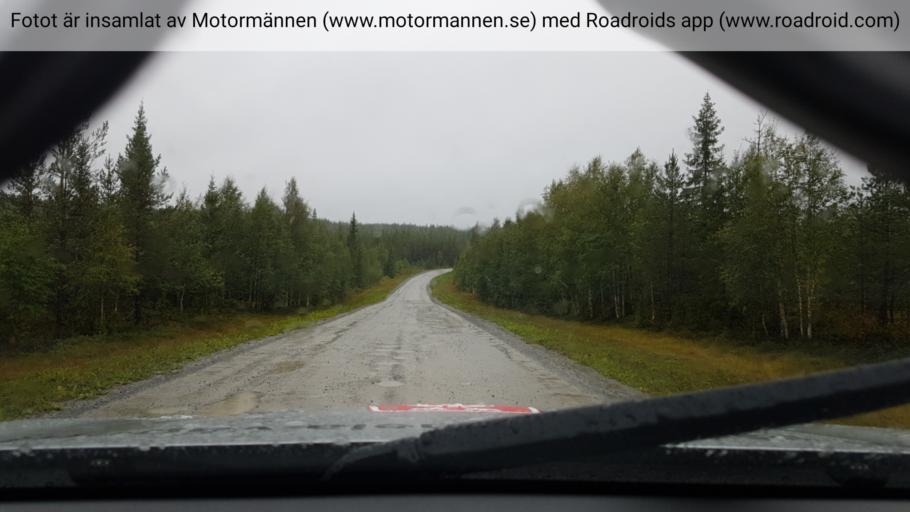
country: SE
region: Vaesternorrland
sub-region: OErnskoeldsviks Kommun
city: Bredbyn
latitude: 64.0646
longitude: 18.1018
